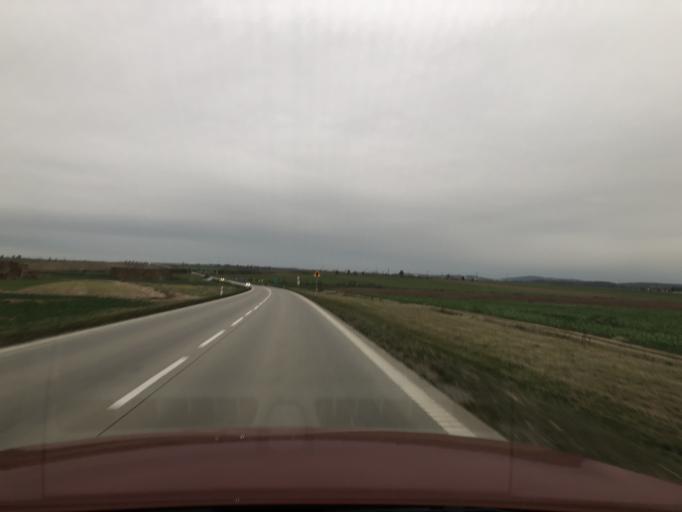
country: PL
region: Lower Silesian Voivodeship
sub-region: Powiat swidnicki
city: Zarow
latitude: 50.9074
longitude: 16.4809
